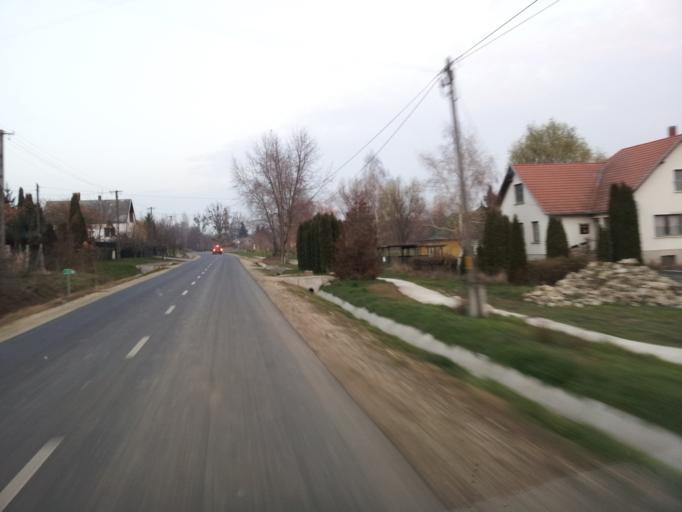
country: HU
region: Zala
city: Zalaszentgrot
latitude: 46.8934
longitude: 17.1519
